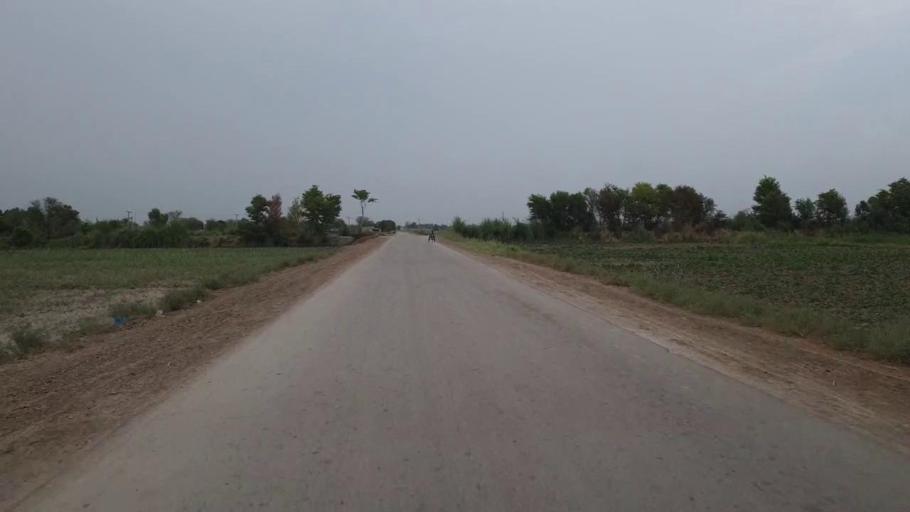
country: PK
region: Sindh
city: Bandhi
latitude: 26.5351
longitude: 68.2194
